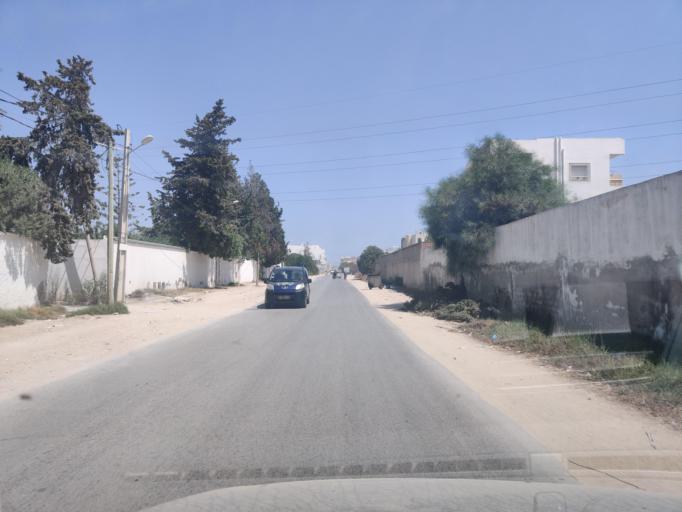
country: TN
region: Tunis
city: Al Marsa
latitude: 36.8687
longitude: 10.2923
